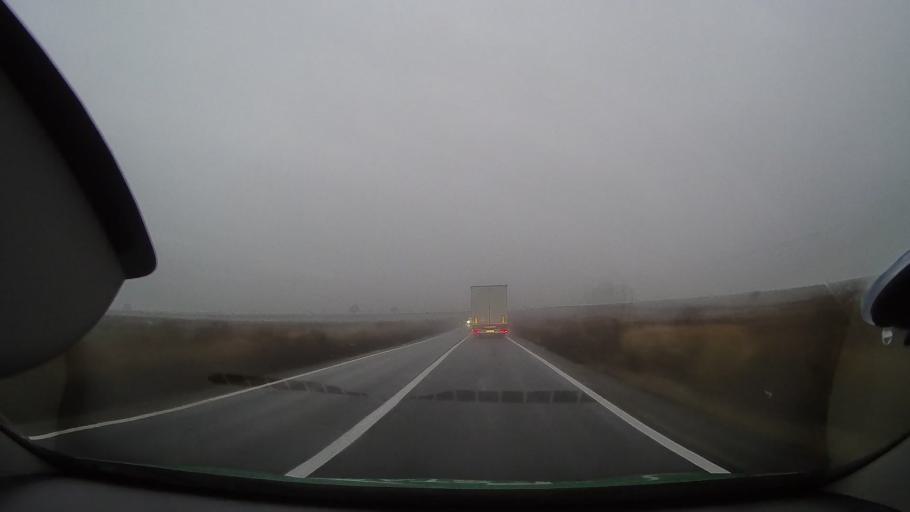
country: RO
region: Bihor
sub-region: Comuna Olcea
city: Olcea
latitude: 46.6695
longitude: 21.9641
